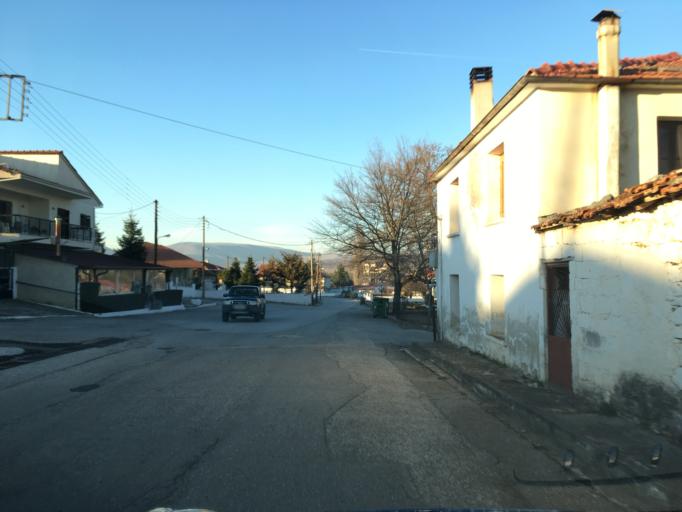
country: GR
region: West Macedonia
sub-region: Nomos Kozanis
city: Kozani
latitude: 40.2857
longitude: 21.7332
